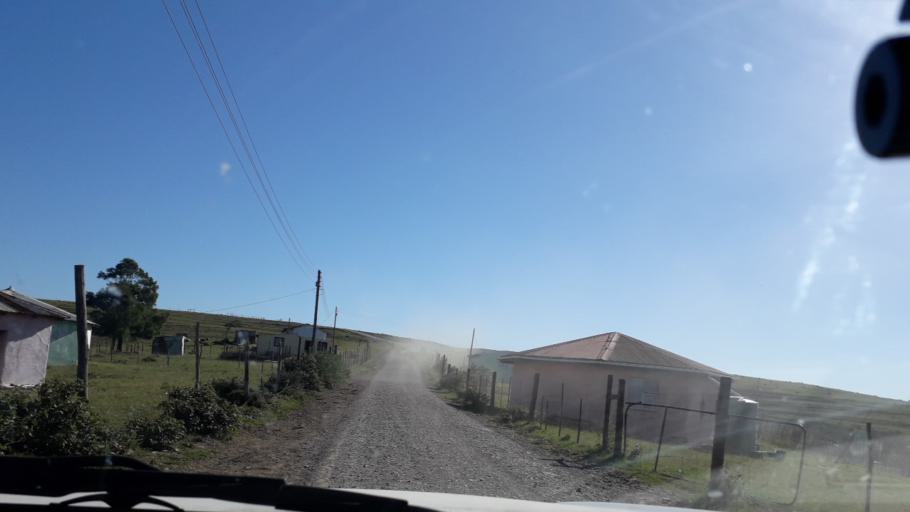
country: ZA
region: Eastern Cape
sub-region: Buffalo City Metropolitan Municipality
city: East London
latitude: -32.7987
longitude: 27.9570
